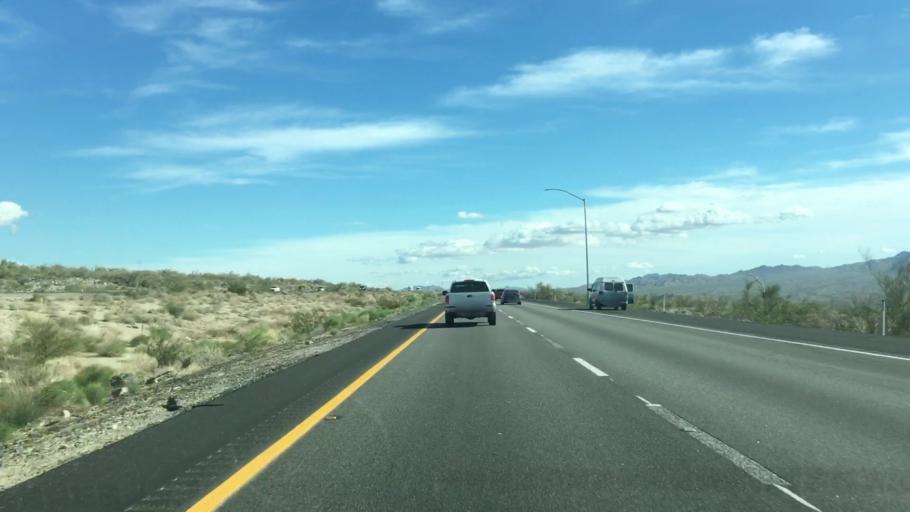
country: US
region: California
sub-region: Riverside County
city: Mecca
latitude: 33.6691
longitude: -115.9105
